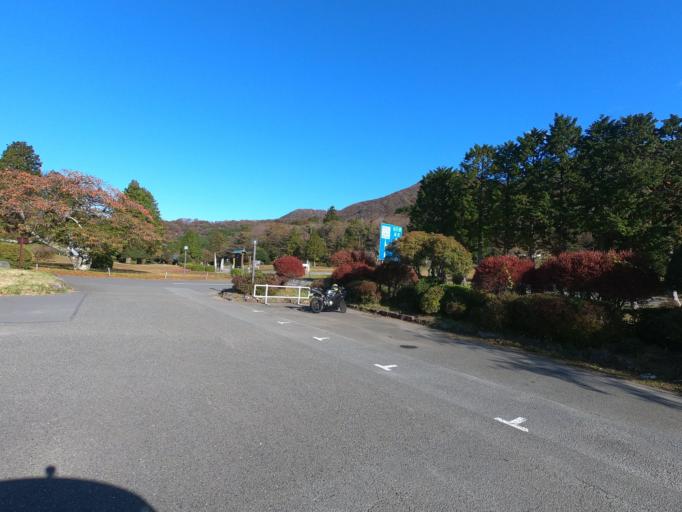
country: JP
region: Kanagawa
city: Hakone
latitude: 35.2100
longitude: 139.0123
